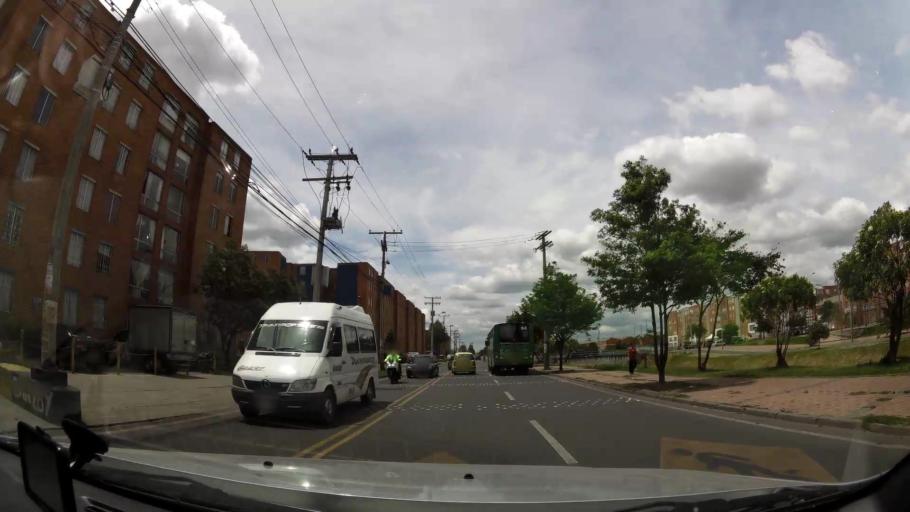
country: CO
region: Bogota D.C.
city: Bogota
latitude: 4.6474
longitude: -74.1561
